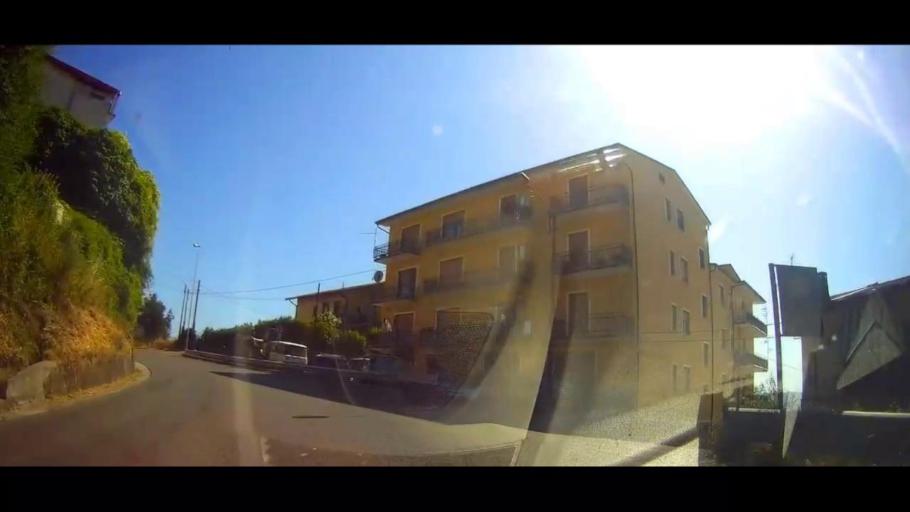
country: IT
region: Calabria
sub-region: Provincia di Cosenza
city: Celico
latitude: 39.3080
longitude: 16.3414
